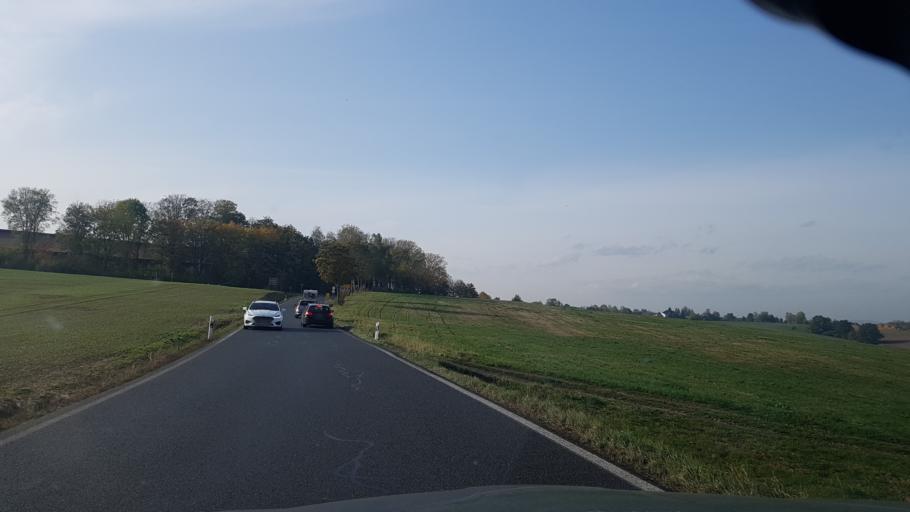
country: DE
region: Saxony
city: Struppen
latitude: 50.9295
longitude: 14.0264
